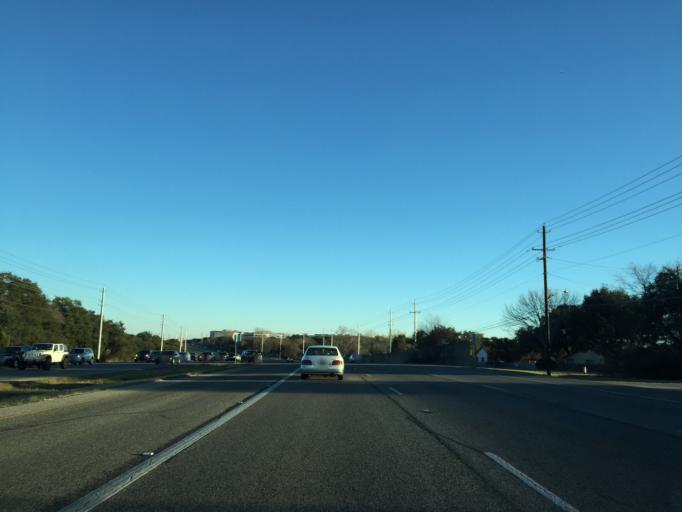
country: US
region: Texas
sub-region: Williamson County
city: Jollyville
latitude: 30.4419
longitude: -97.7414
